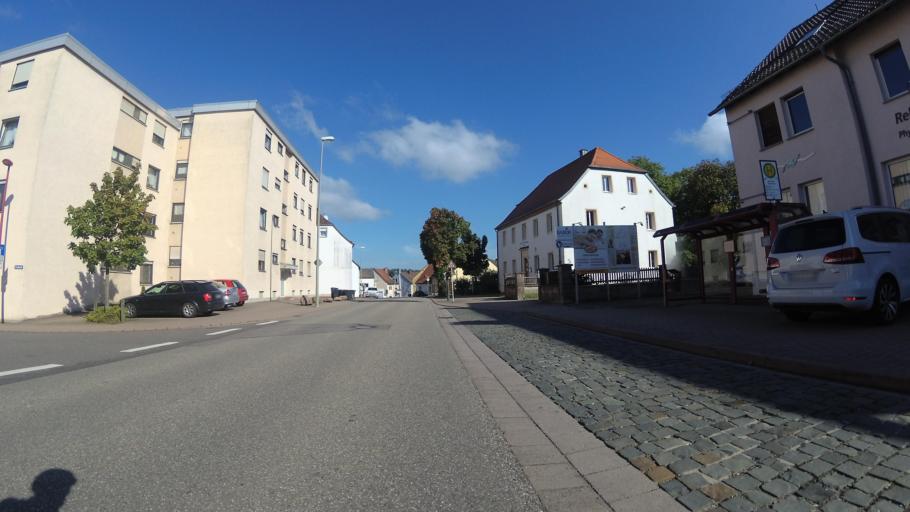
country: DE
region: Rheinland-Pfalz
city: Waldmohr
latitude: 49.3849
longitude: 7.3319
